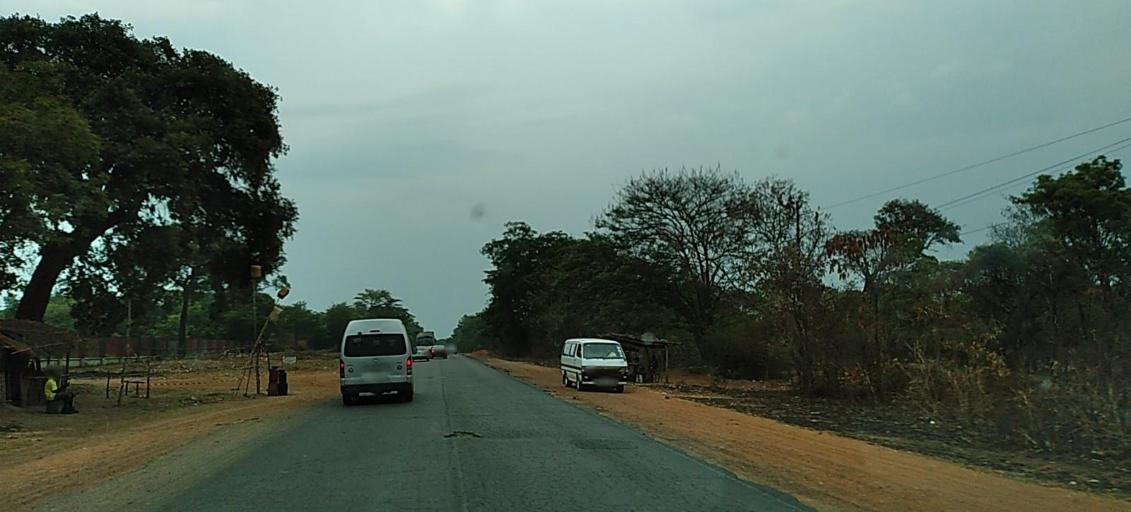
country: ZM
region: Copperbelt
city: Luanshya
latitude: -13.0827
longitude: 28.4429
